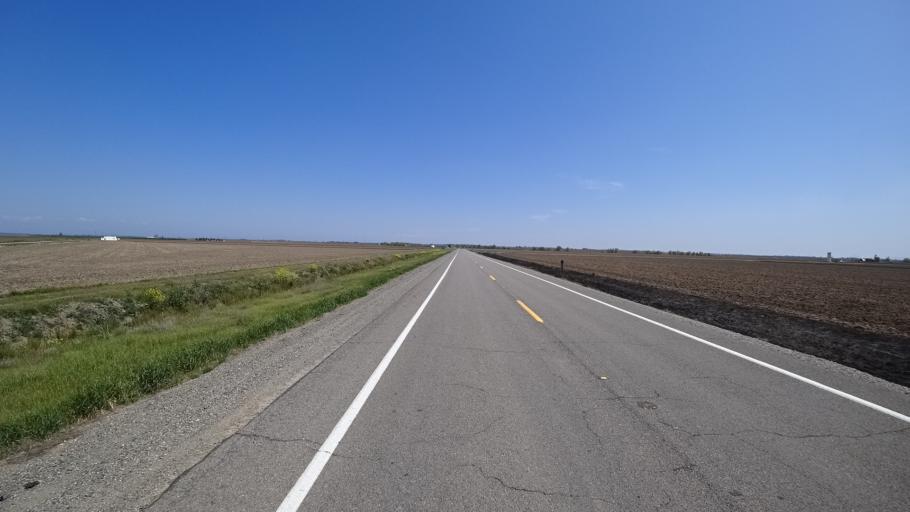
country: US
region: California
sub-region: Glenn County
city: Willows
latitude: 39.5219
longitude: -122.0450
